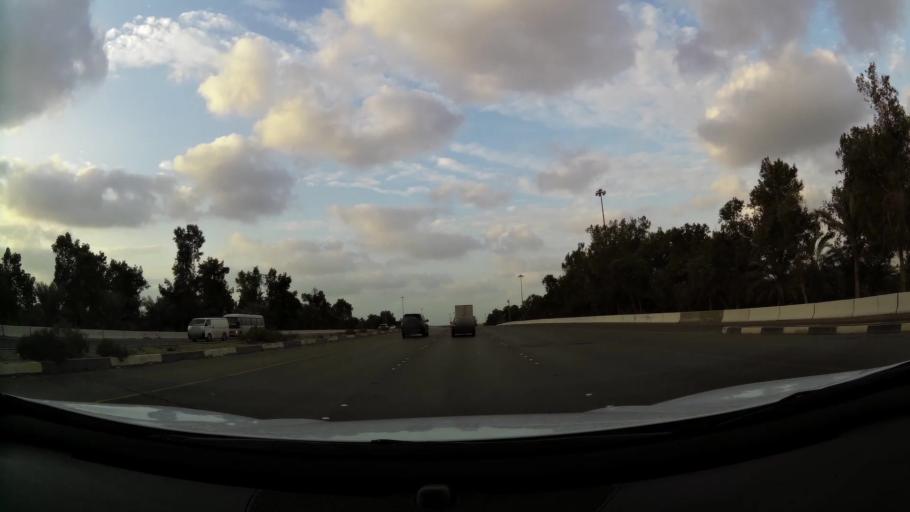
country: AE
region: Abu Dhabi
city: Abu Dhabi
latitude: 24.3913
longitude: 54.5241
